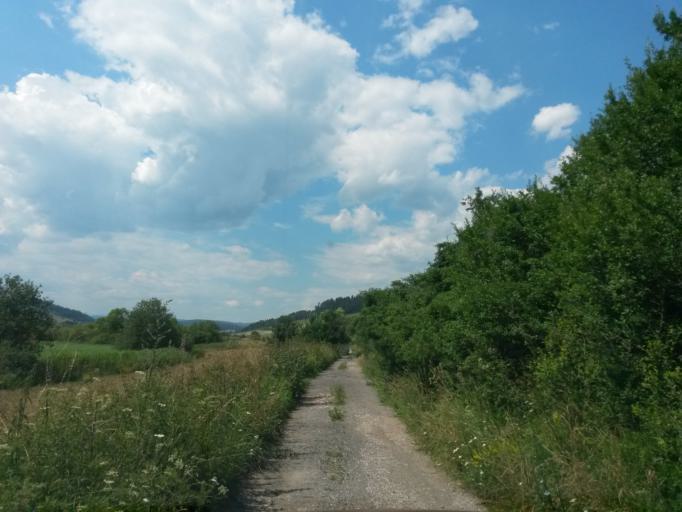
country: SK
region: Kosicky
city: Spisska Nova Ves
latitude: 48.9406
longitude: 20.6025
